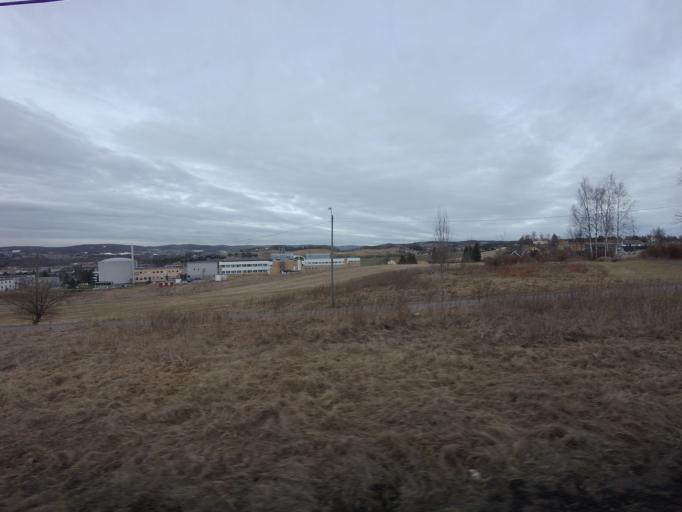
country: NO
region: Akershus
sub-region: Skedsmo
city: Lillestrom
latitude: 59.9747
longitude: 11.0563
